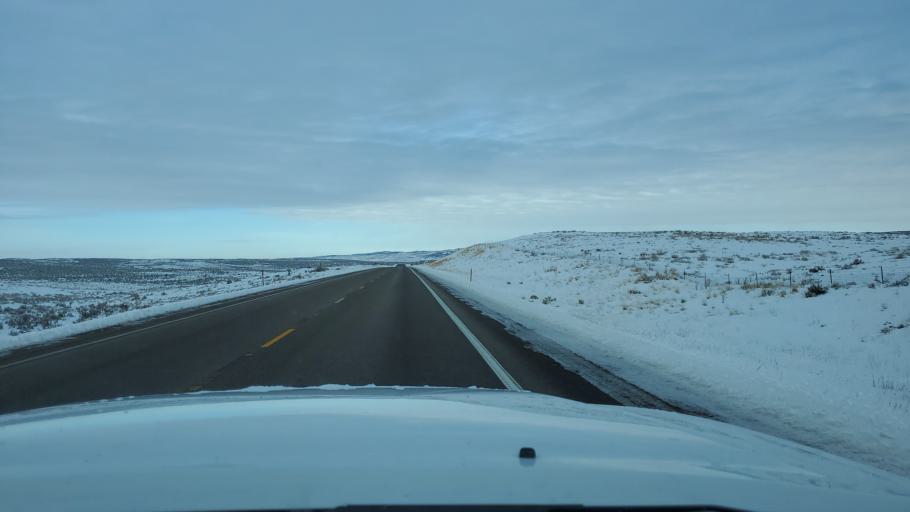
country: US
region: Colorado
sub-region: Moffat County
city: Craig
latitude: 40.5234
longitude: -107.7577
